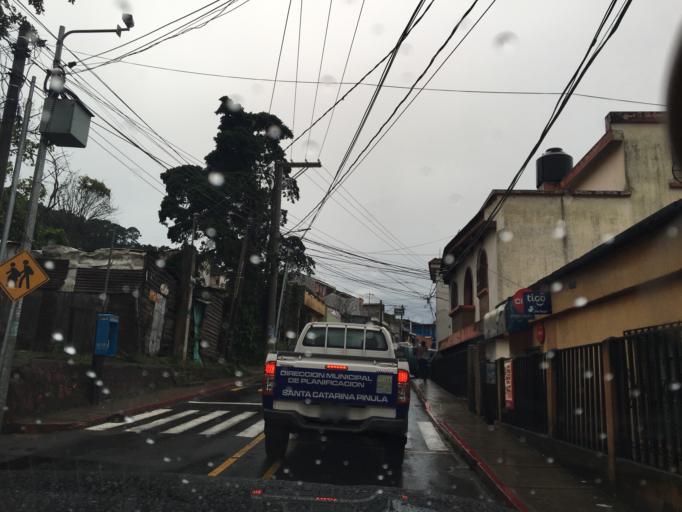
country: GT
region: Guatemala
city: Santa Catarina Pinula
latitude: 14.5618
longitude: -90.4896
